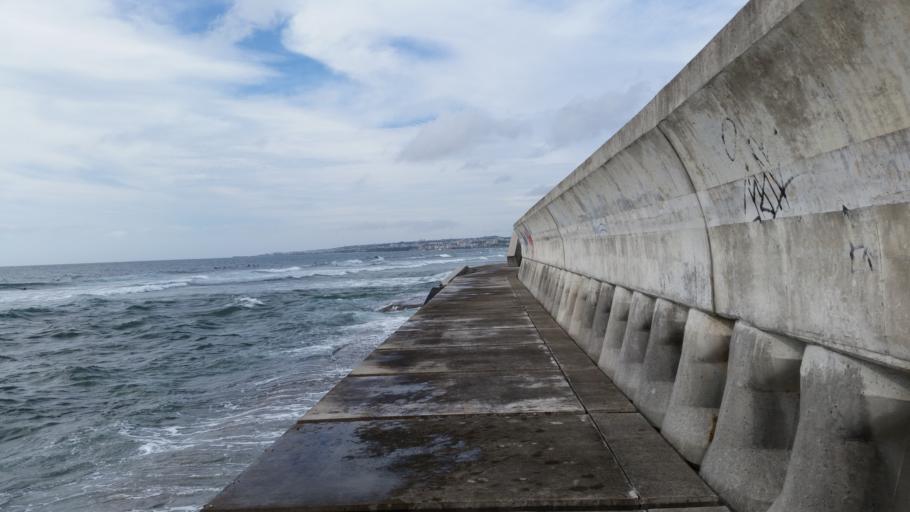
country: JP
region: Okinawa
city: Chatan
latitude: 26.3330
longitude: 127.7426
